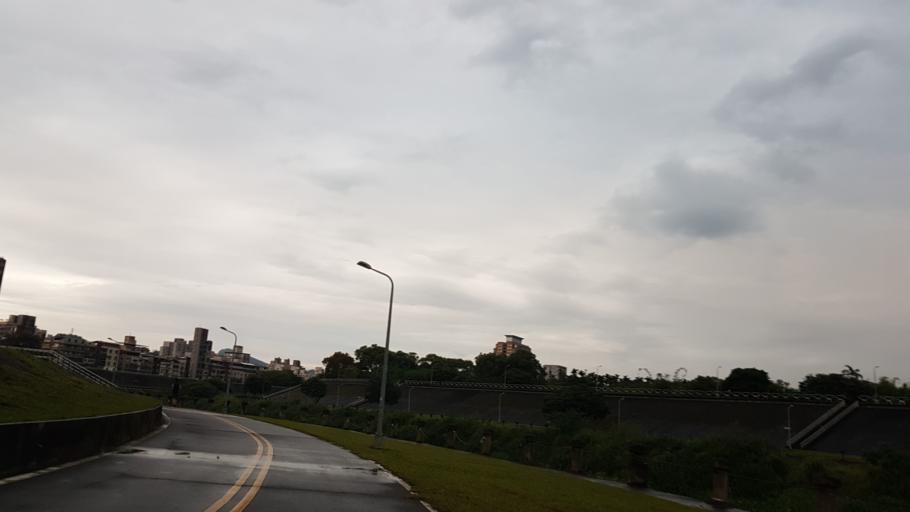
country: TW
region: Taipei
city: Taipei
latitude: 24.9771
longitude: 121.5570
